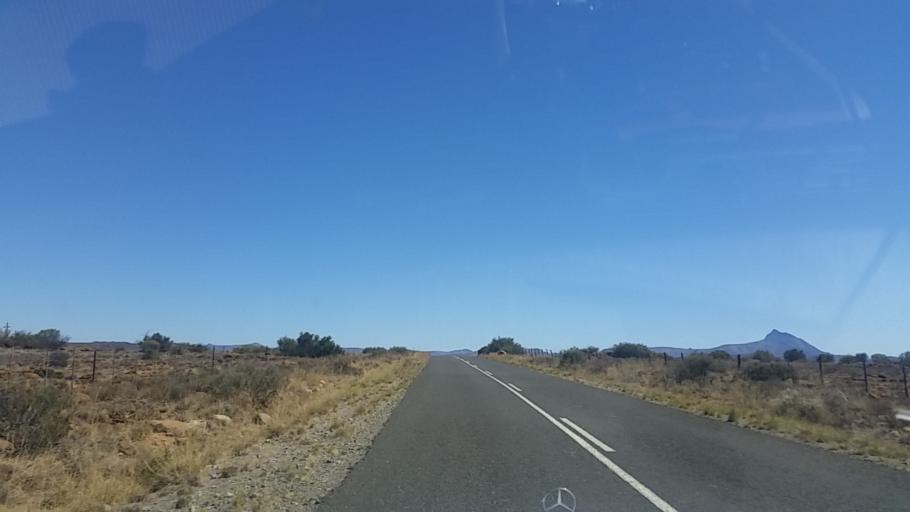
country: ZA
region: Eastern Cape
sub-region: Cacadu District Municipality
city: Graaff-Reinet
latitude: -31.9065
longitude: 24.5941
